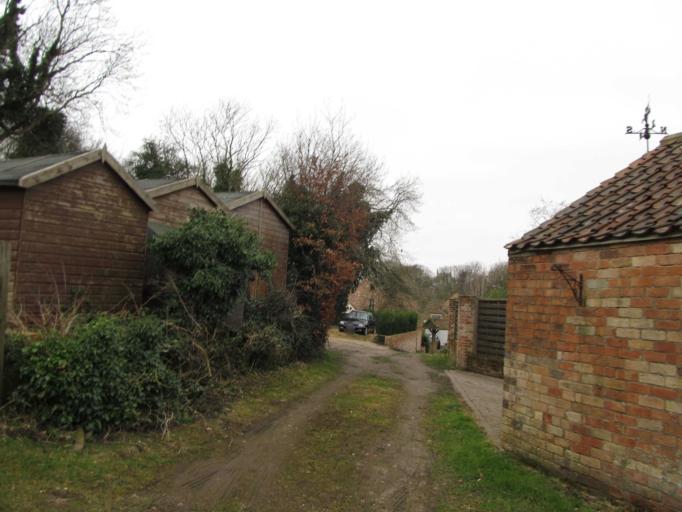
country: GB
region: England
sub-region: Nottinghamshire
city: Misterton
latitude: 53.4079
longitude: -0.8905
